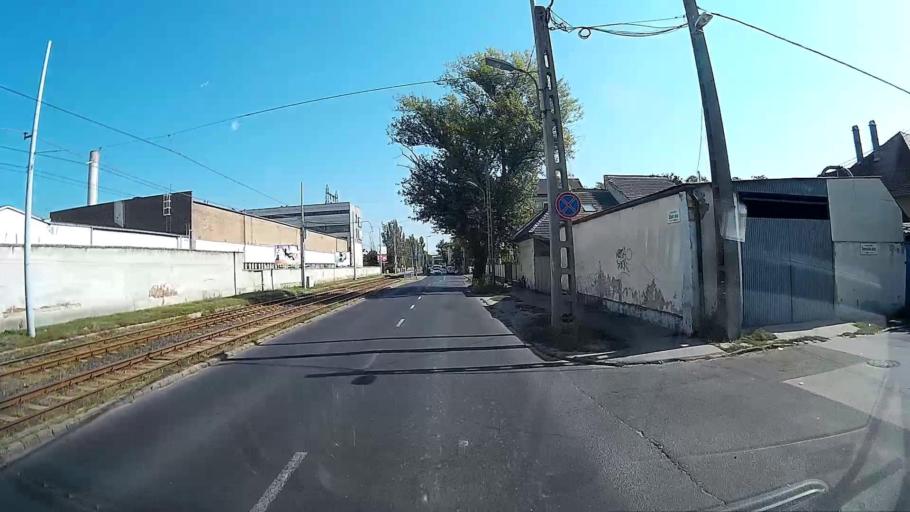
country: HU
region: Budapest
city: Budapest XIX. keruelet
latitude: 47.4750
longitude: 19.1178
